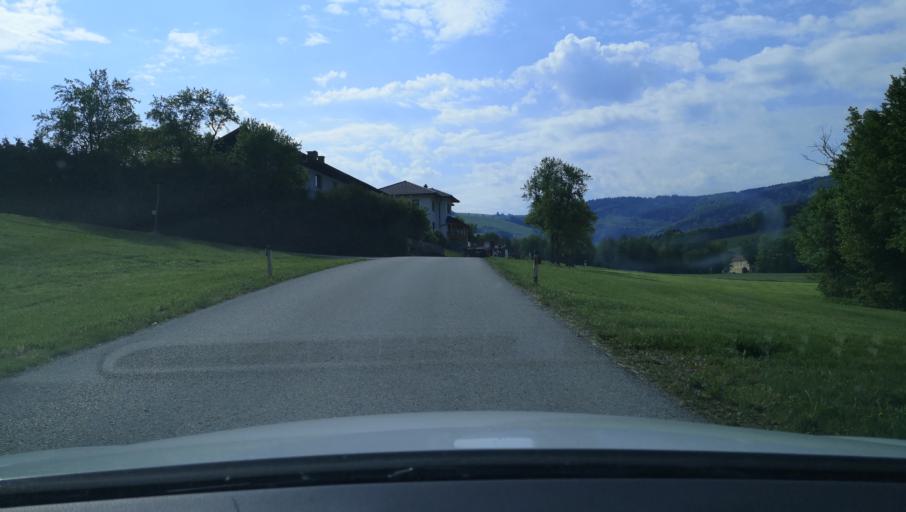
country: AT
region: Lower Austria
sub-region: Politischer Bezirk Amstetten
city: Neuhofen an der Ybbs
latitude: 48.0505
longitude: 14.8825
